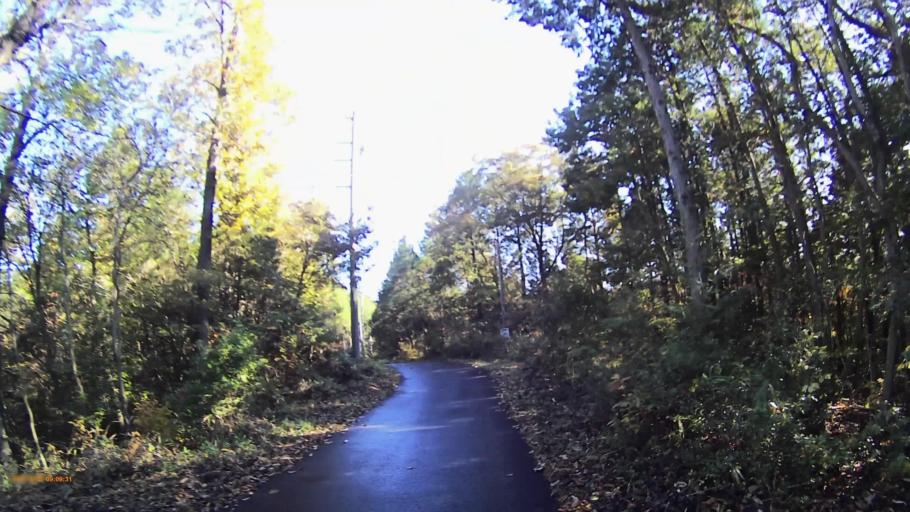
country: JP
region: Gifu
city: Mizunami
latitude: 35.4399
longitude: 137.3524
